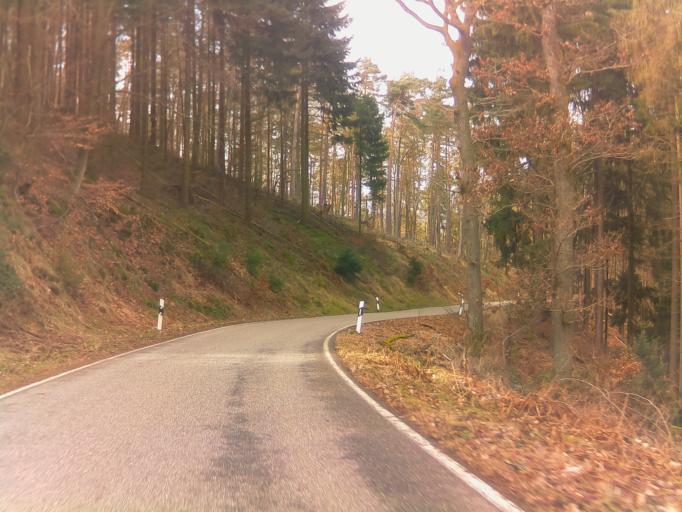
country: DE
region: Rheinland-Pfalz
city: Ramberg
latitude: 49.2995
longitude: 8.0272
